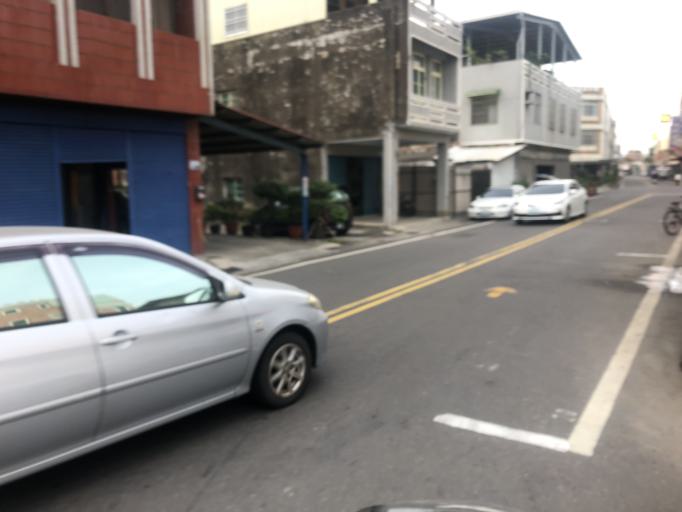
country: TW
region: Taiwan
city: Xinying
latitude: 23.1847
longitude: 120.2444
